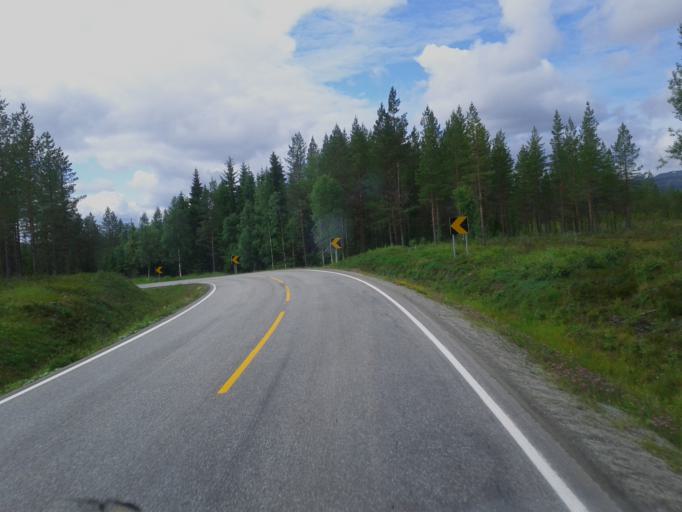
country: NO
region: Nord-Trondelag
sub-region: Hoylandet
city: Hoylandet
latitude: 64.6481
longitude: 12.6372
